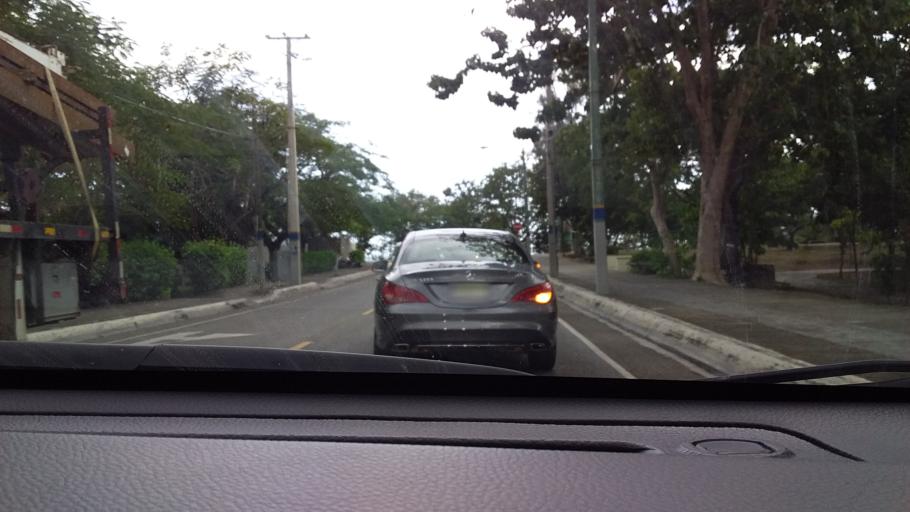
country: DO
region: Nacional
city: Bella Vista
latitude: 18.4529
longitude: -69.9353
